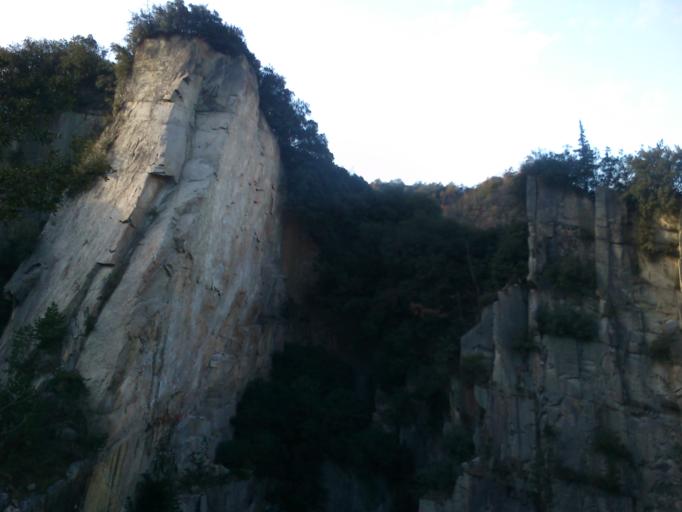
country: JP
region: Okayama
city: Kasaoka
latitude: 34.3877
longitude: 133.5316
